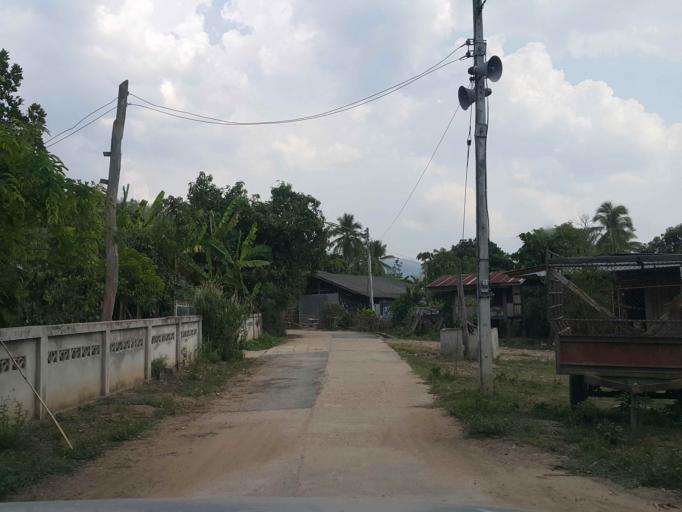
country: TH
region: Chiang Mai
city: Wiang Haeng
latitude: 19.3973
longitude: 98.7212
